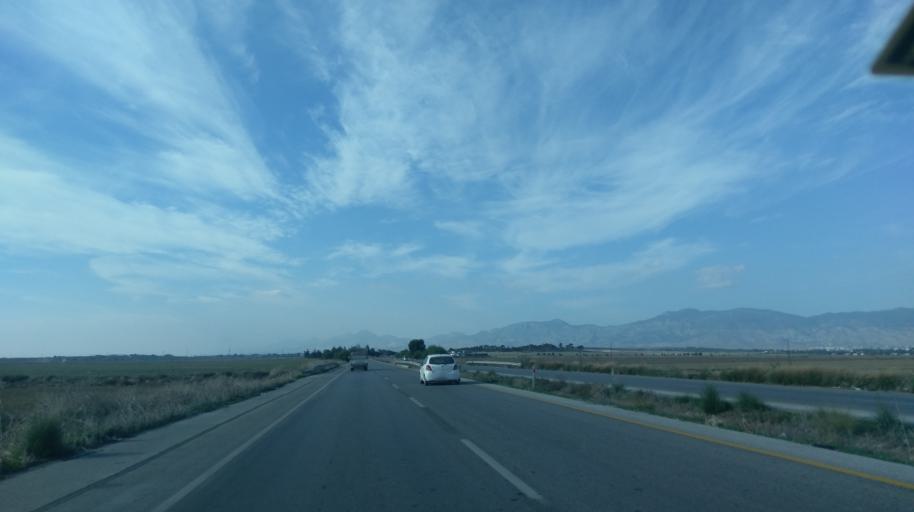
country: CY
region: Ammochostos
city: Lefkonoiko
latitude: 35.1903
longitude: 33.6273
